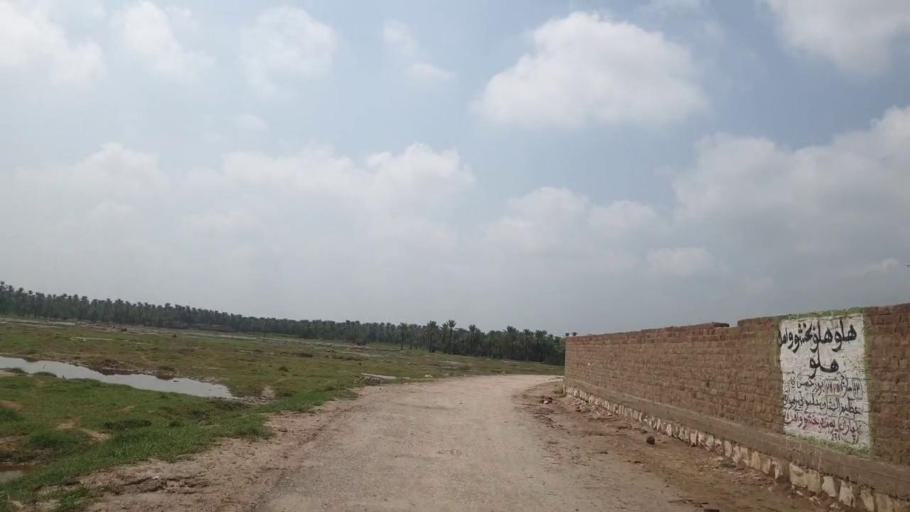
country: PK
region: Sindh
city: Pir jo Goth
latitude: 27.6240
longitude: 68.6788
